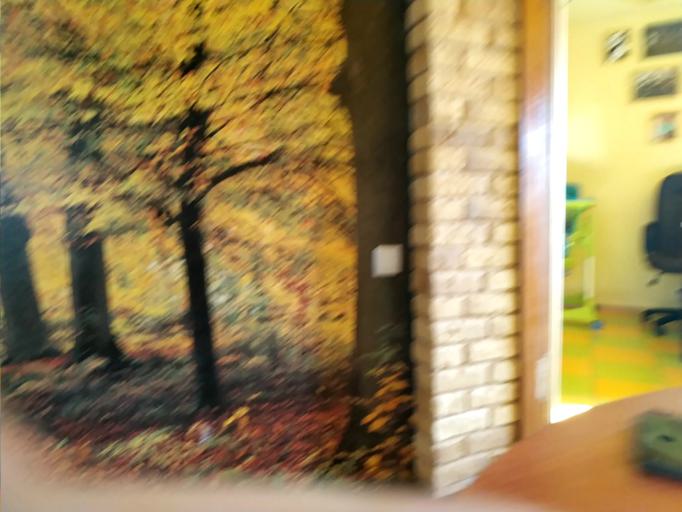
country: RU
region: Novgorod
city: Parfino
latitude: 57.7651
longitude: 31.7526
